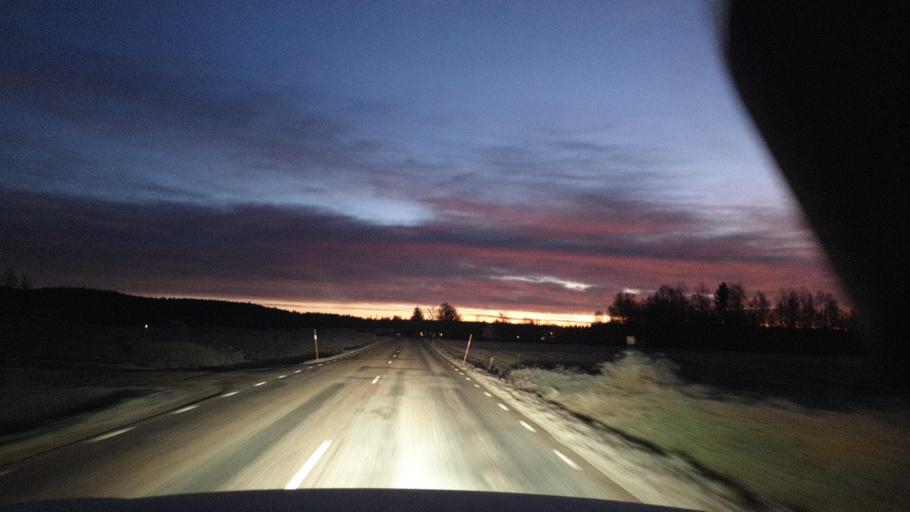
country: SE
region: Vaermland
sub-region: Eda Kommun
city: Charlottenberg
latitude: 59.9211
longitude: 12.2766
